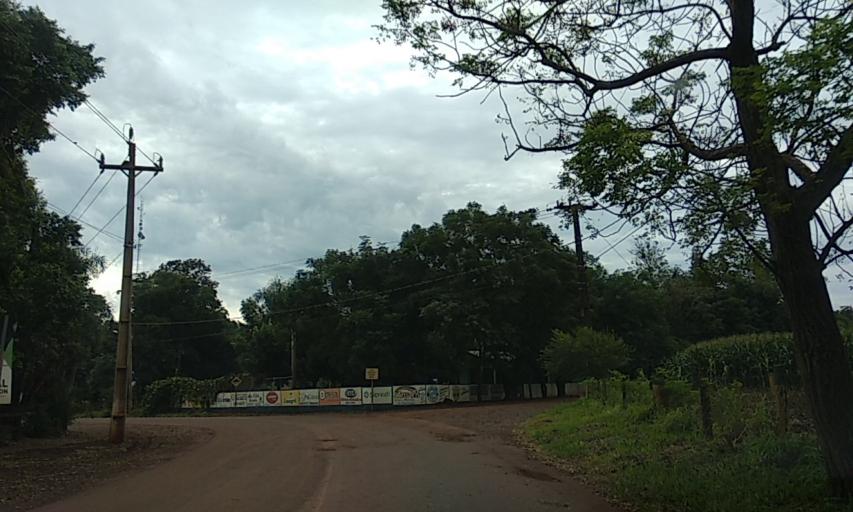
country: BR
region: Parana
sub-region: Marechal Candido Rondon
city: Marechal Candido Rondon
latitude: -24.5415
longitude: -54.0951
